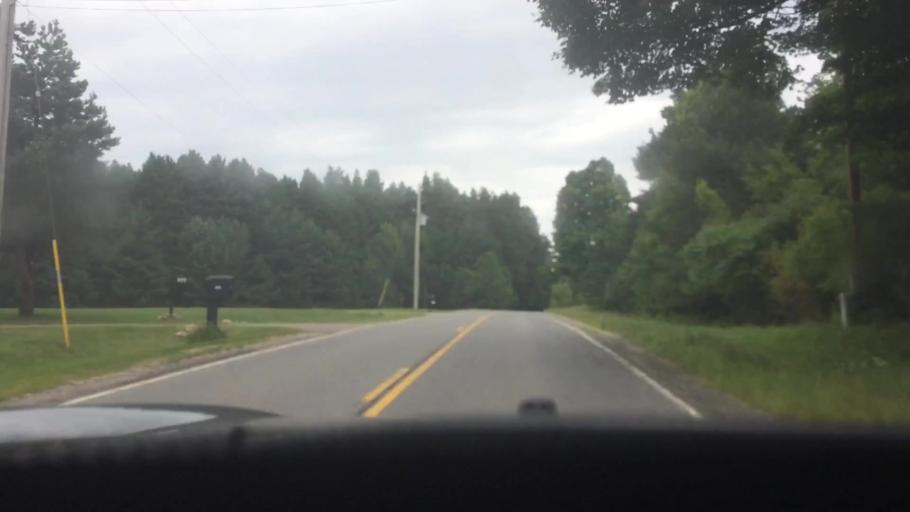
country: US
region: New York
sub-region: St. Lawrence County
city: Hannawa Falls
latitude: 44.5965
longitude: -74.8877
